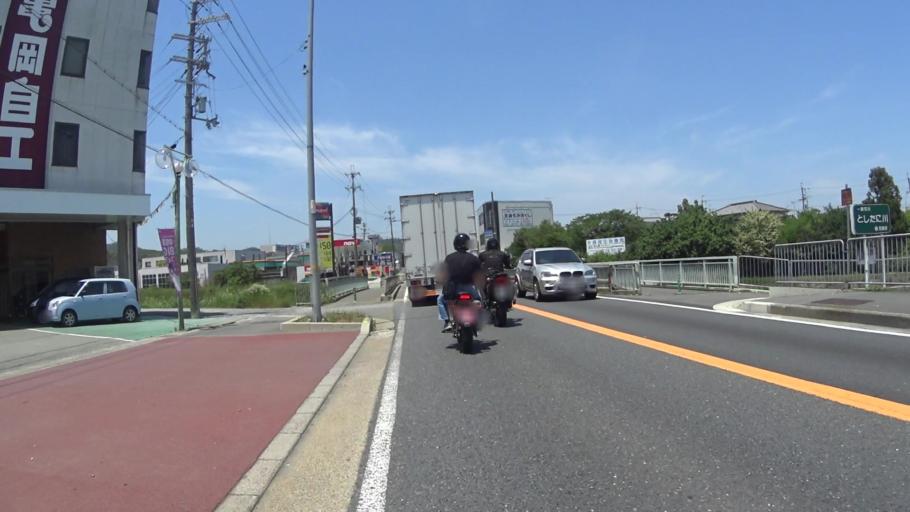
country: JP
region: Kyoto
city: Kameoka
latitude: 35.0044
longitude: 135.5879
